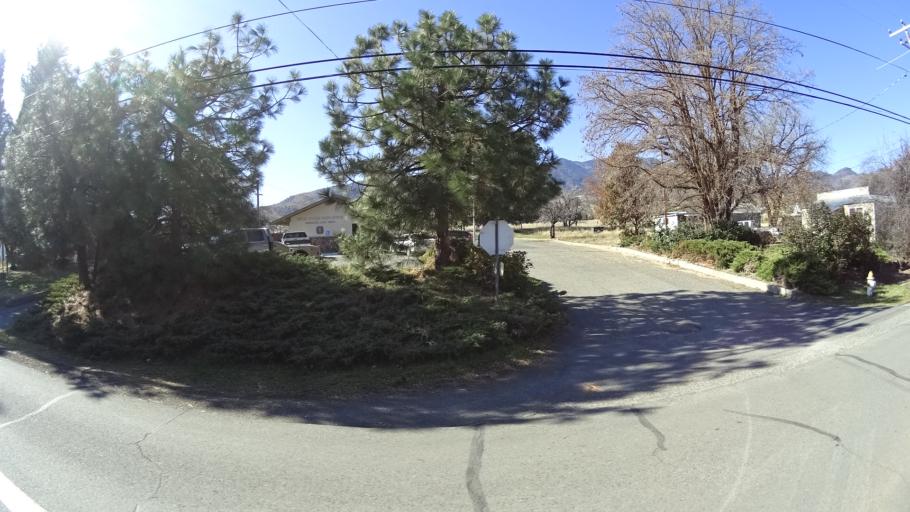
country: US
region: California
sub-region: Siskiyou County
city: Montague
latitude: 41.9080
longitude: -122.5577
